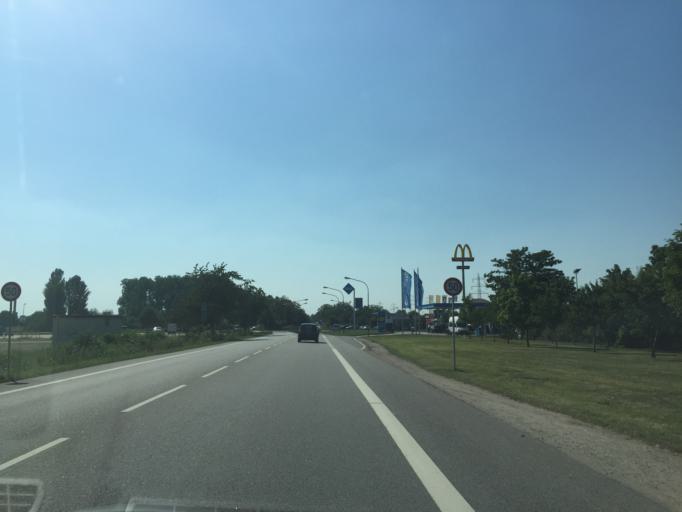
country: DE
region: Hesse
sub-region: Regierungsbezirk Darmstadt
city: Heppenheim an der Bergstrasse
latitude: 49.6432
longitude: 8.6270
